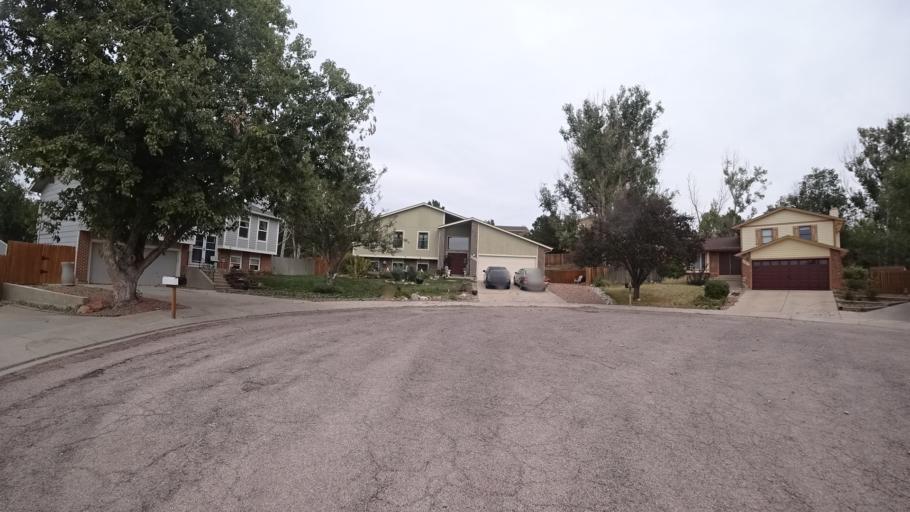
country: US
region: Colorado
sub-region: El Paso County
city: Cimarron Hills
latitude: 38.9042
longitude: -104.7326
